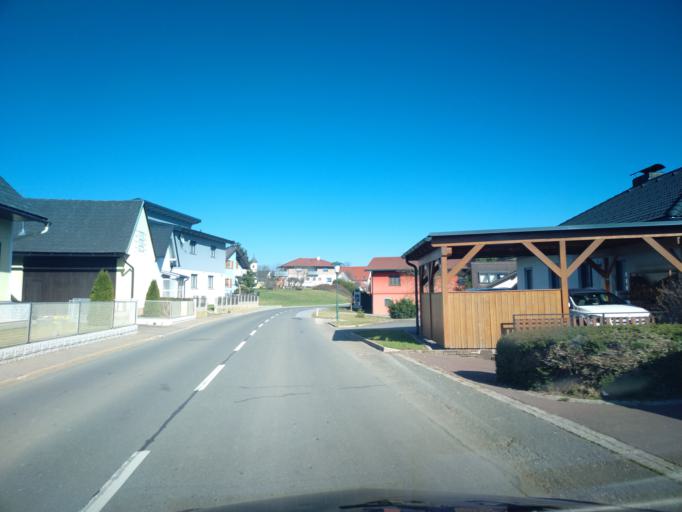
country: AT
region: Styria
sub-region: Politischer Bezirk Leibnitz
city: Weitendorf
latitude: 46.8968
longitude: 15.4631
